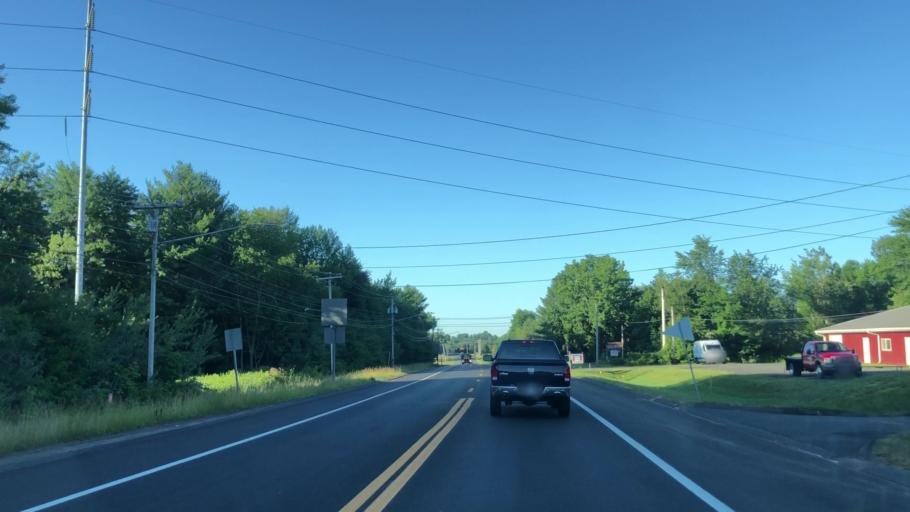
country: US
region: Massachusetts
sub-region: Hampshire County
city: Southampton
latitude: 42.1817
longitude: -72.7266
